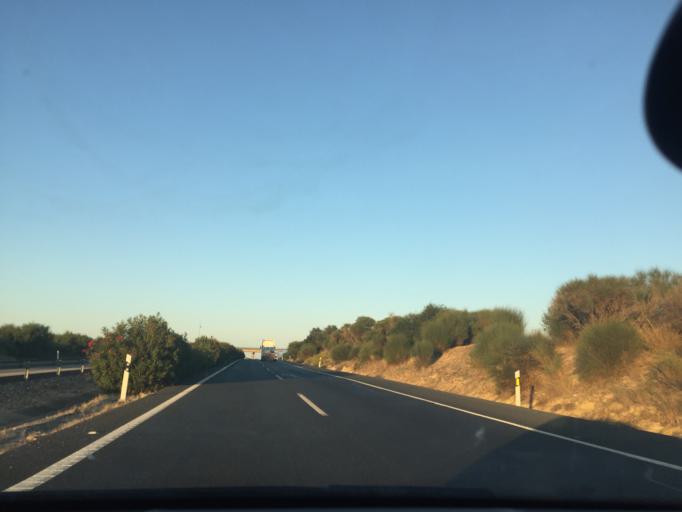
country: ES
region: Andalusia
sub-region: Provincia de Sevilla
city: Carmona
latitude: 37.4750
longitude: -5.6746
